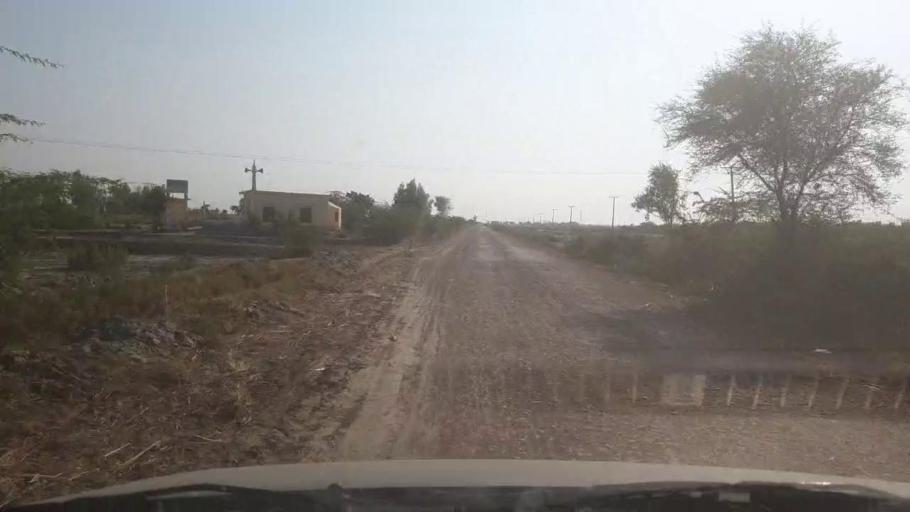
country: PK
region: Sindh
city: Samaro
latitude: 25.1481
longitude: 69.3809
